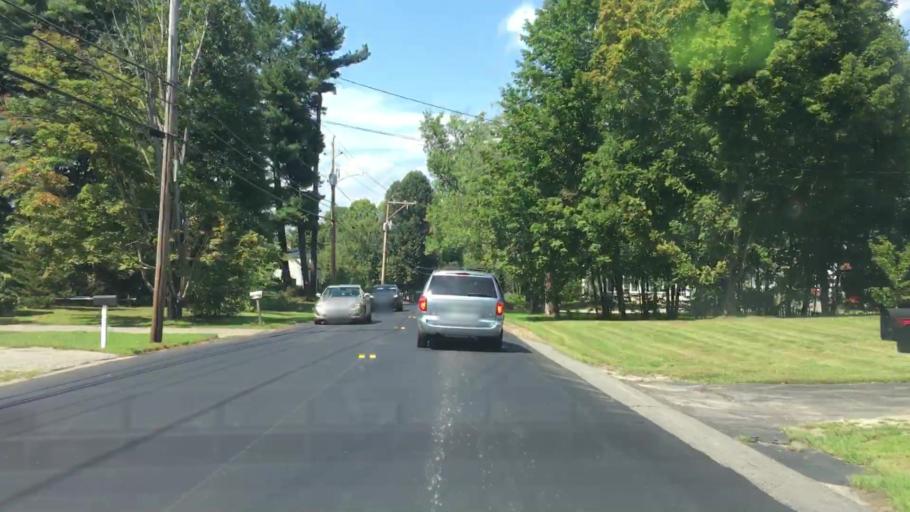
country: US
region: New Hampshire
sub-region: Rockingham County
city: Hampstead
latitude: 42.8950
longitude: -71.2117
